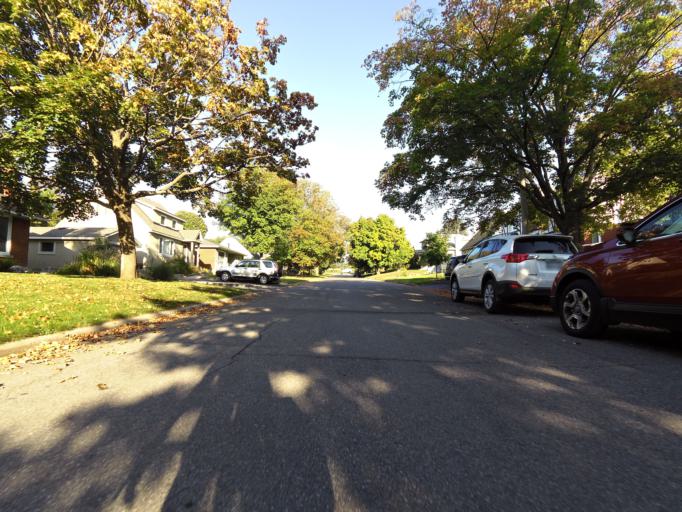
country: CA
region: Ontario
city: Ottawa
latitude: 45.3839
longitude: -75.6690
